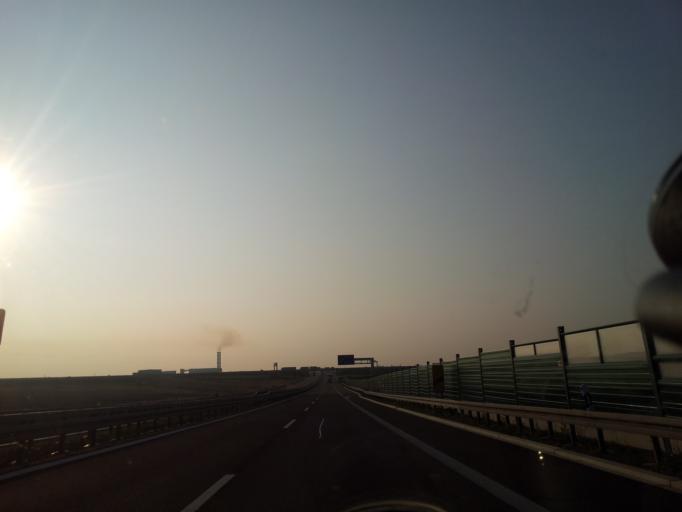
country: DE
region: Saxony-Anhalt
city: Ilberstedt
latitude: 51.8071
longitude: 11.6757
